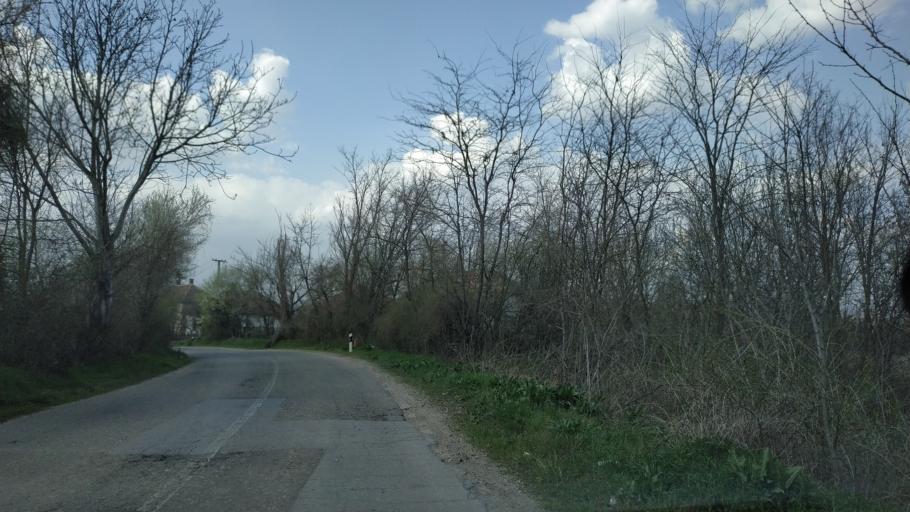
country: RS
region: Central Serbia
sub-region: Nisavski Okrug
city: Razanj
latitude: 43.5762
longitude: 21.5760
